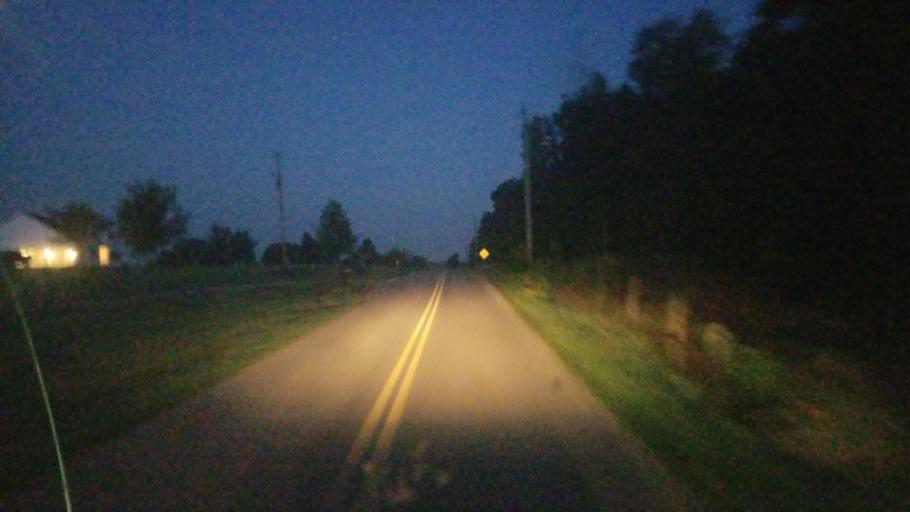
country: US
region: Ohio
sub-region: Perry County
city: Thornport
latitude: 39.9201
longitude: -82.3747
